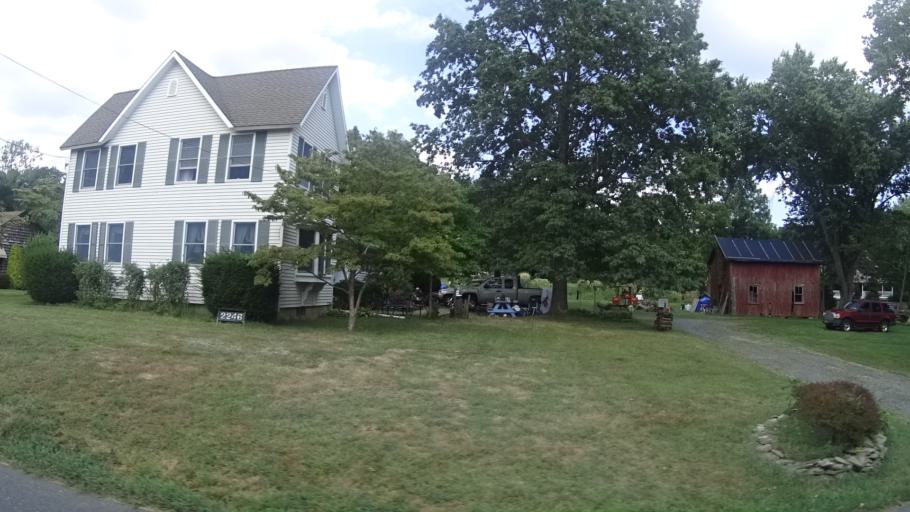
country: US
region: New Jersey
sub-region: Monmouth County
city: Manasquan
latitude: 40.1364
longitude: -74.0948
